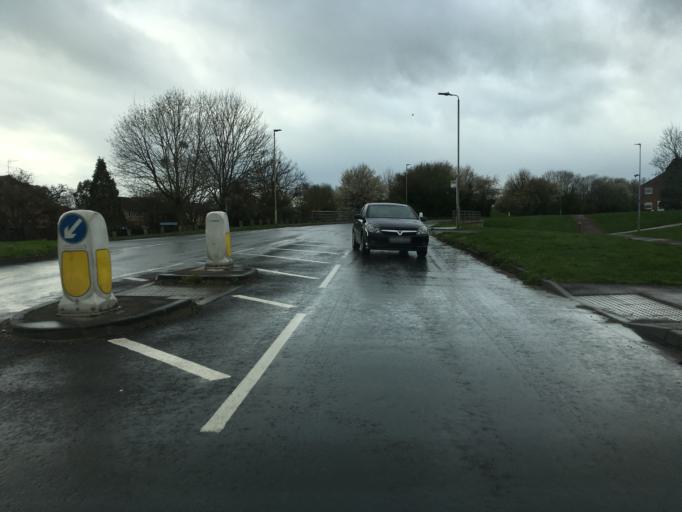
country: GB
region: England
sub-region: Gloucestershire
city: Gloucester
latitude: 51.8193
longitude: -2.2864
